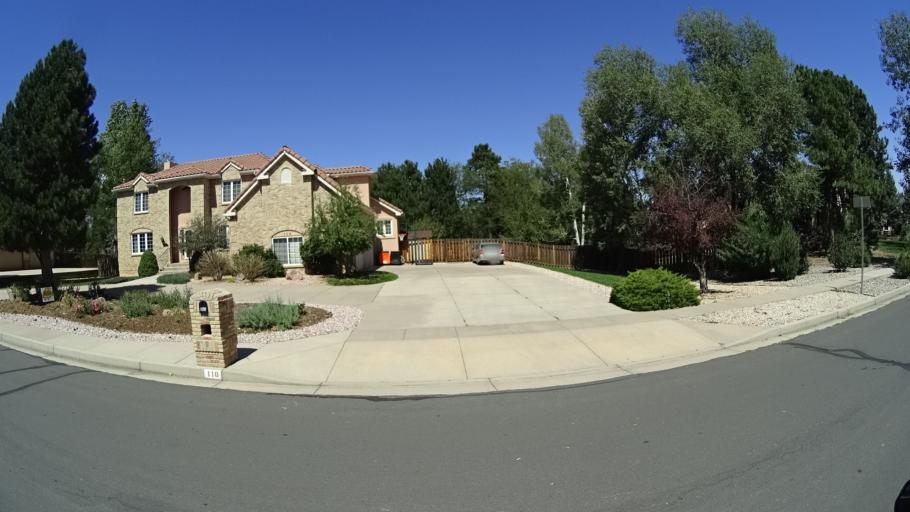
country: US
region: Colorado
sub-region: El Paso County
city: Colorado Springs
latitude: 38.7865
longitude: -104.8297
